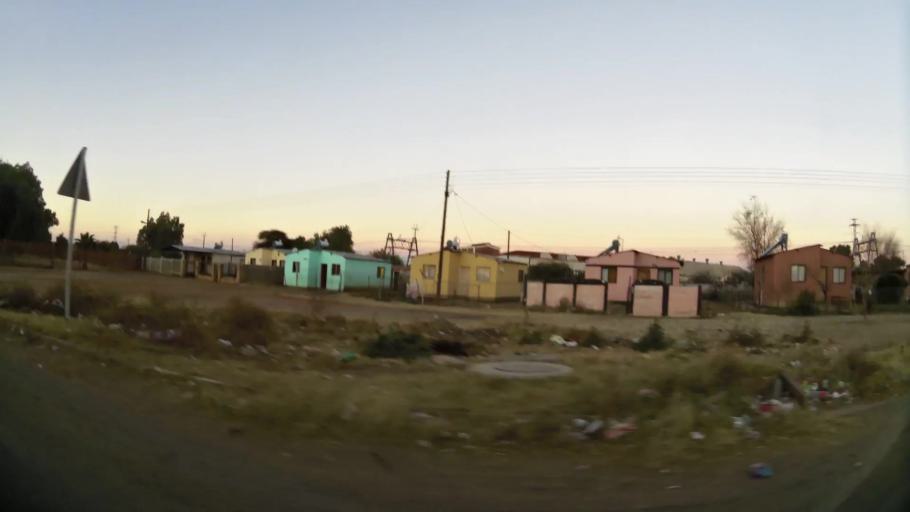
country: ZA
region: Northern Cape
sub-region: Frances Baard District Municipality
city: Kimberley
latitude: -28.7139
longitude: 24.7686
